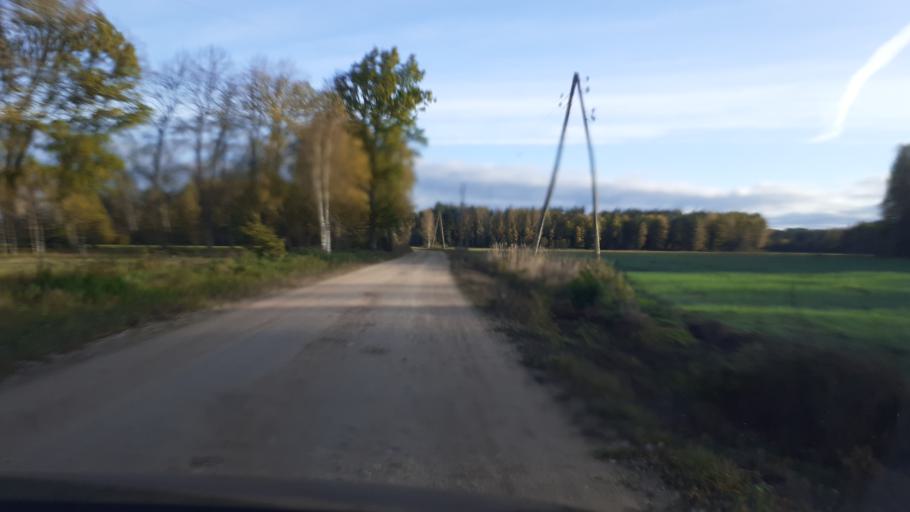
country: LV
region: Kuldigas Rajons
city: Kuldiga
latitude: 56.8754
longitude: 22.1053
